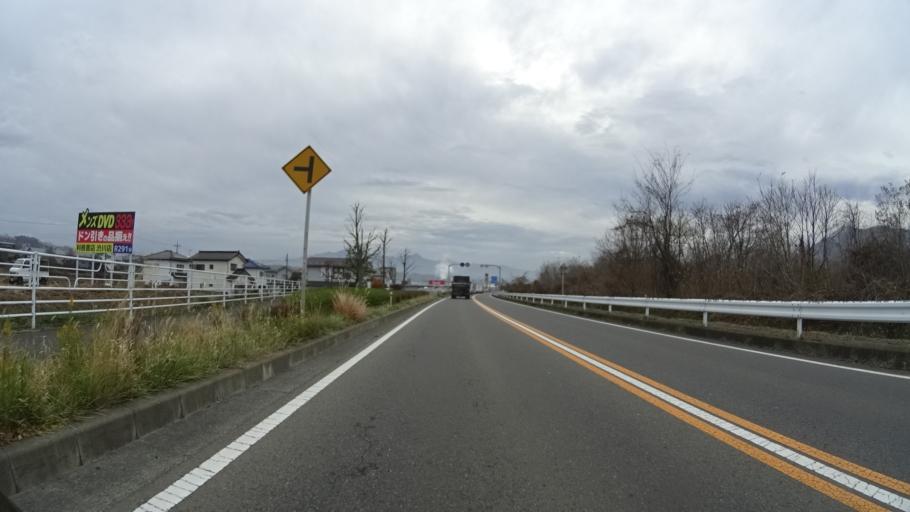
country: JP
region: Gunma
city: Numata
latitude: 36.6602
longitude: 139.0174
